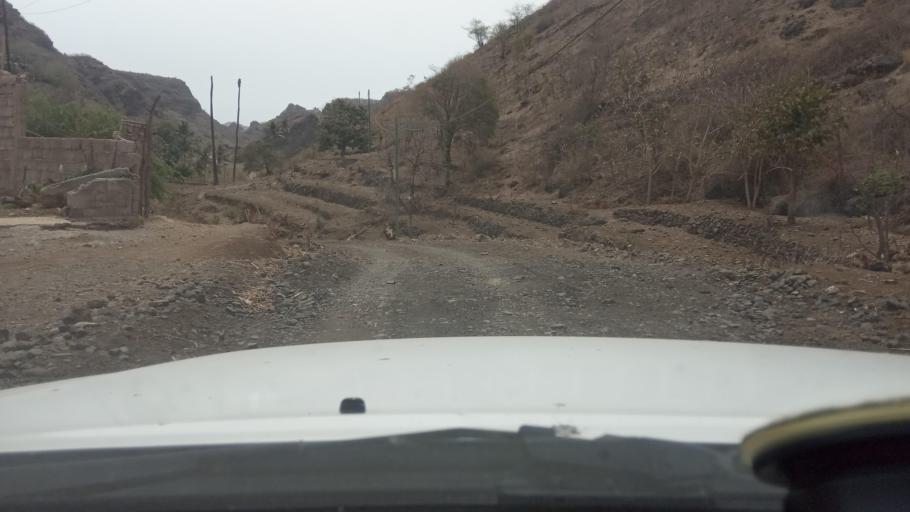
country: CV
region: Sao Salvador do Mundo
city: Picos
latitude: 15.1225
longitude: -23.6246
